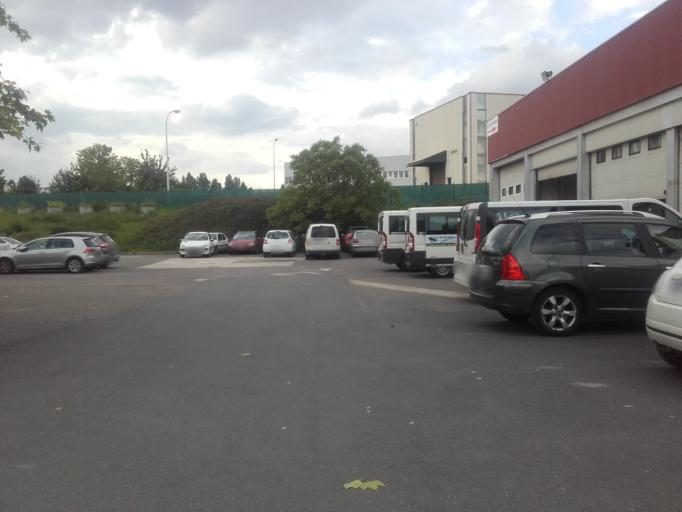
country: FR
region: Ile-de-France
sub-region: Departement du Val-de-Marne
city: Orly
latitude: 48.7461
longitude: 2.3871
